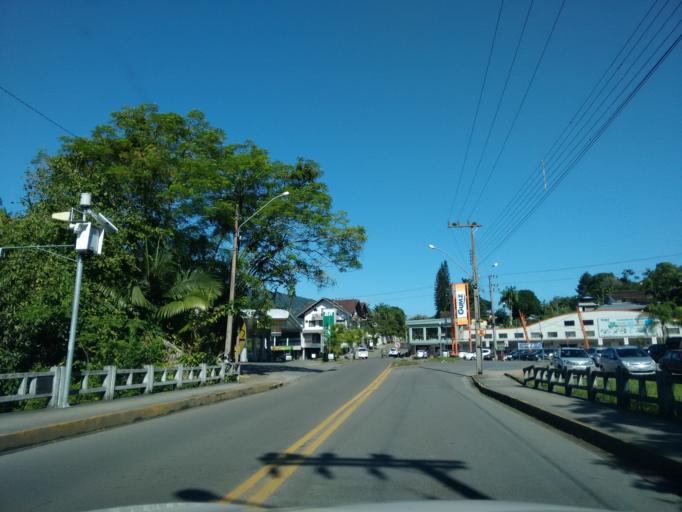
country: BR
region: Santa Catarina
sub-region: Pomerode
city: Pomerode
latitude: -26.7259
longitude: -49.1719
